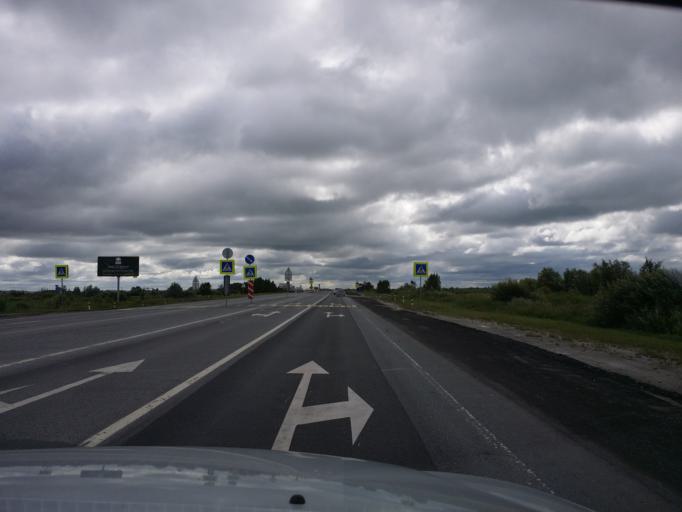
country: RU
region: Tjumen
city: Antipino
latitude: 57.1599
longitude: 65.8089
